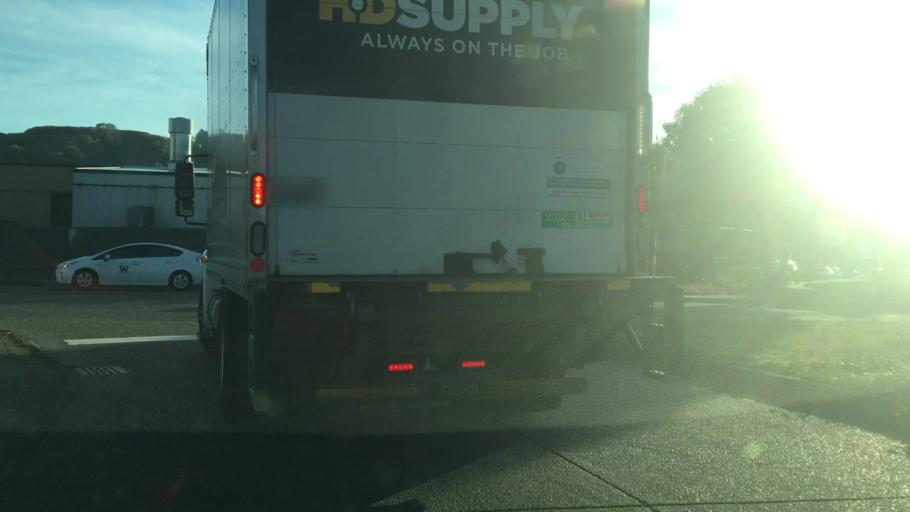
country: US
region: Washington
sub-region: King County
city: Seattle
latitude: 47.5668
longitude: -122.3271
